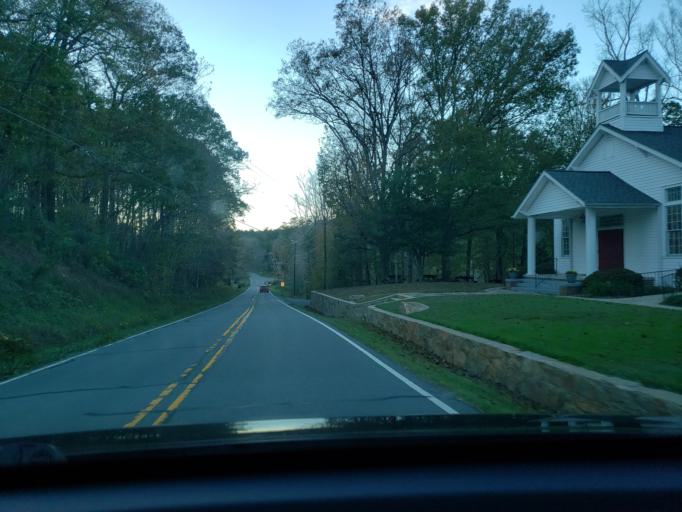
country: US
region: North Carolina
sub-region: Stokes County
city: Danbury
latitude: 36.4095
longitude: -80.2110
